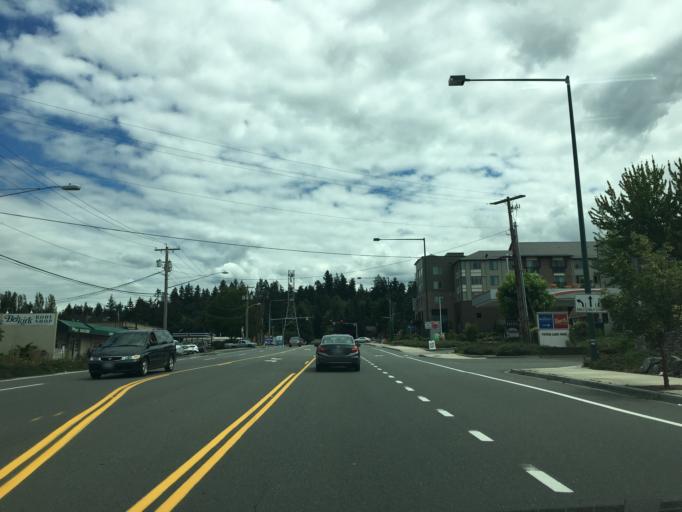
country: US
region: Washington
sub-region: King County
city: Kingsgate
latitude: 47.7039
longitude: -122.1780
